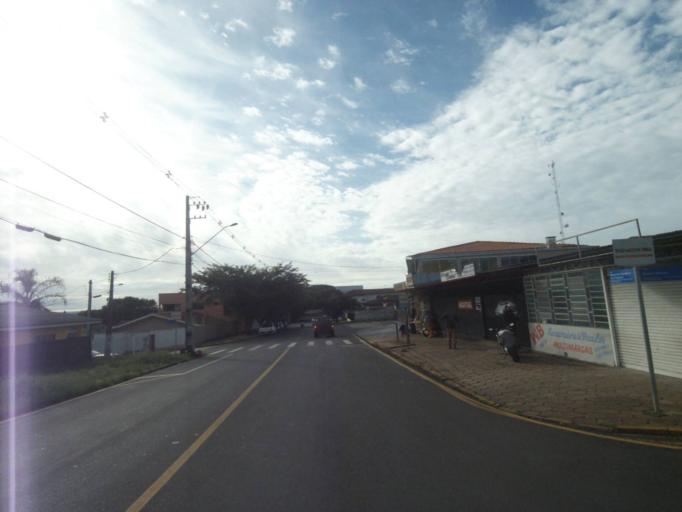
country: BR
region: Parana
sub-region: Telemaco Borba
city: Telemaco Borba
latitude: -24.3362
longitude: -50.6270
